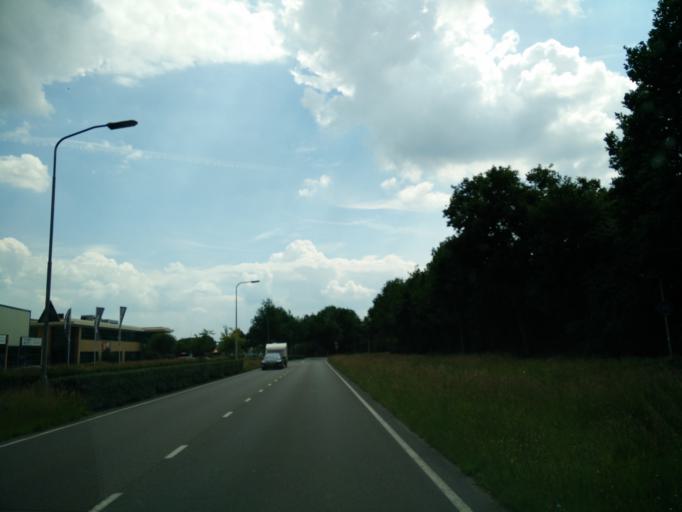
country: NL
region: Drenthe
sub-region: Gemeente Assen
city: Assen
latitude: 53.0117
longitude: 6.5894
